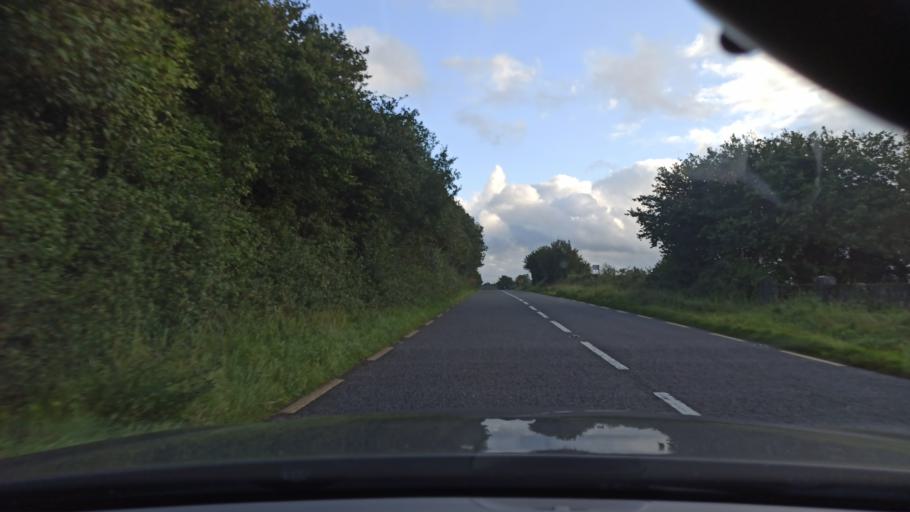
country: IE
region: Munster
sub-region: North Tipperary
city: Roscrea
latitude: 52.8763
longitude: -7.8087
